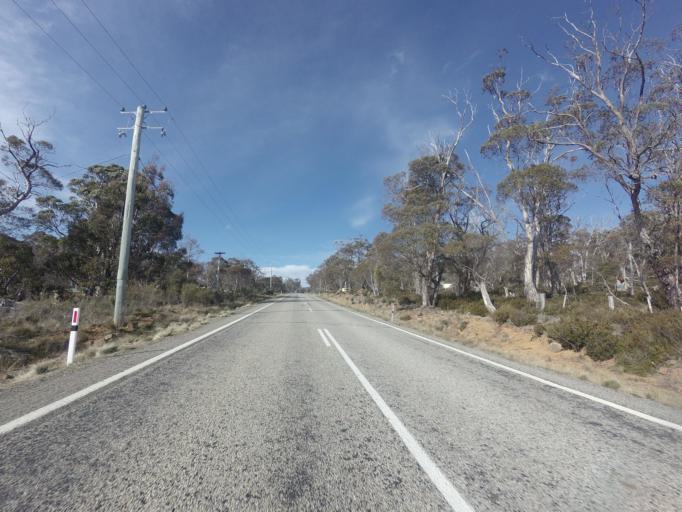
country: AU
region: Tasmania
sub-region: Meander Valley
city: Deloraine
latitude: -41.9904
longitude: 146.6936
